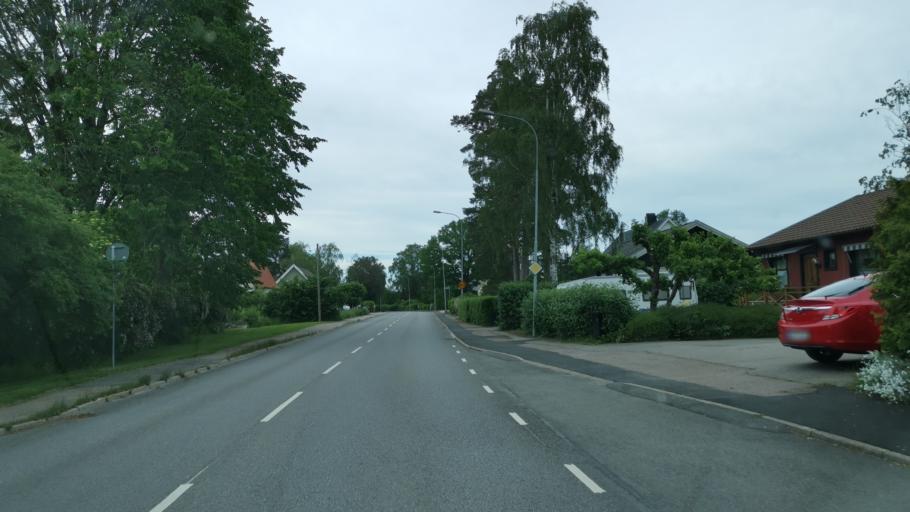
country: SE
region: Vaestra Goetaland
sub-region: Vanersborgs Kommun
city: Vanersborg
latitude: 58.3544
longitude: 12.3505
